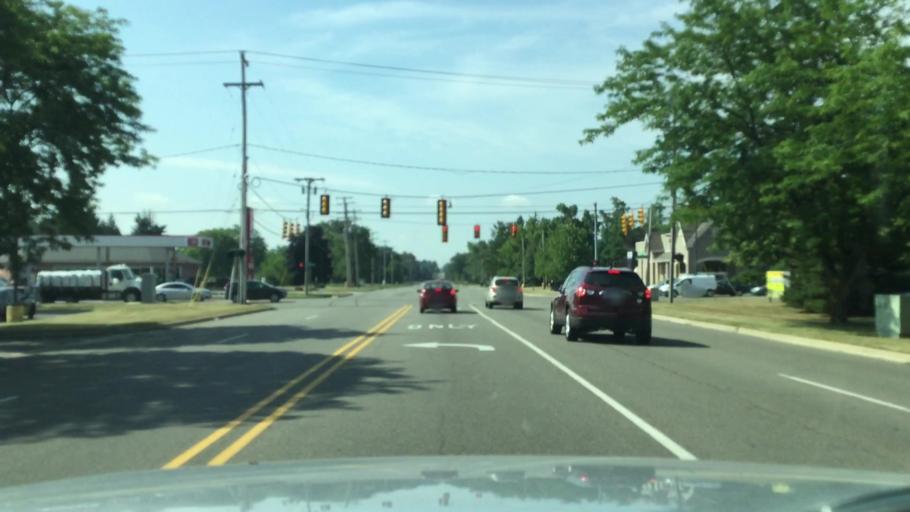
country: US
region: Michigan
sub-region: Genesee County
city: Flushing
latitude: 43.0609
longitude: -83.8132
